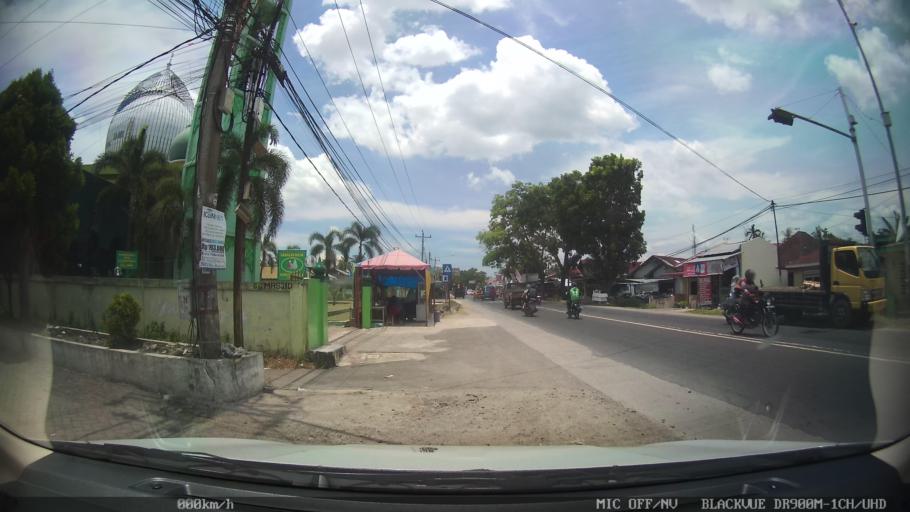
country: ID
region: North Sumatra
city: Binjai
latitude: 3.6278
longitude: 98.5086
